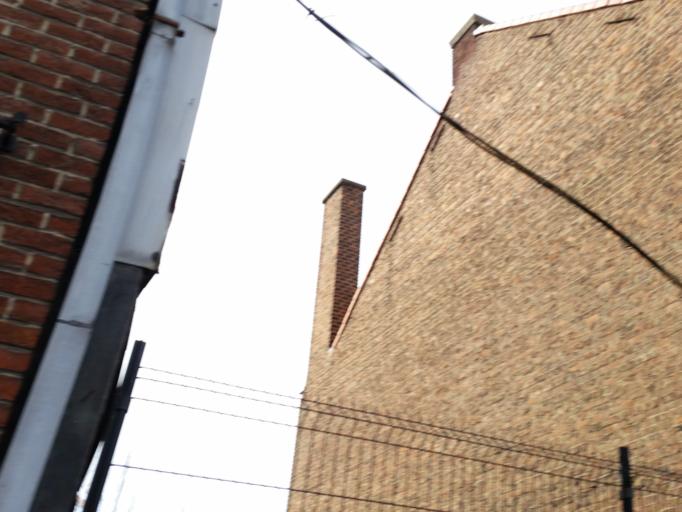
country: BE
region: Flanders
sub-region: Provincie Oost-Vlaanderen
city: Gent
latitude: 51.0357
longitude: 3.7063
